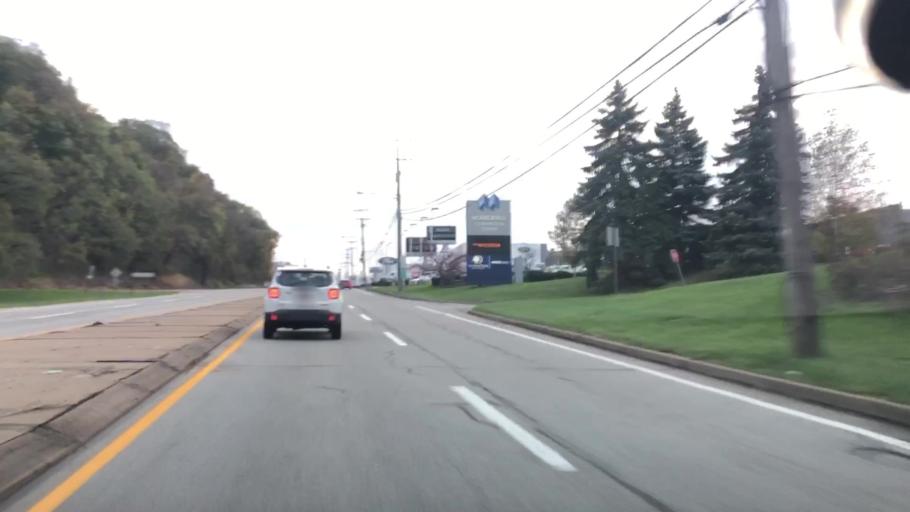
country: US
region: Pennsylvania
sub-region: Allegheny County
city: Monroeville
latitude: 40.4342
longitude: -79.7944
